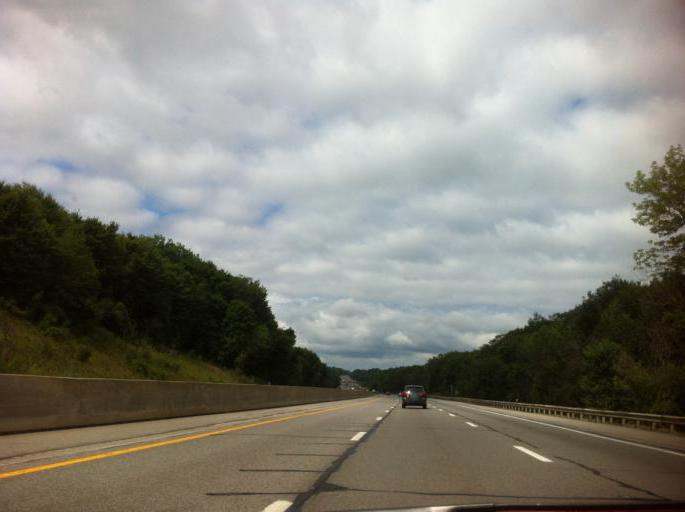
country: US
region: Ohio
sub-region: Portage County
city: Mantua
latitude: 41.2475
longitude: -81.2709
